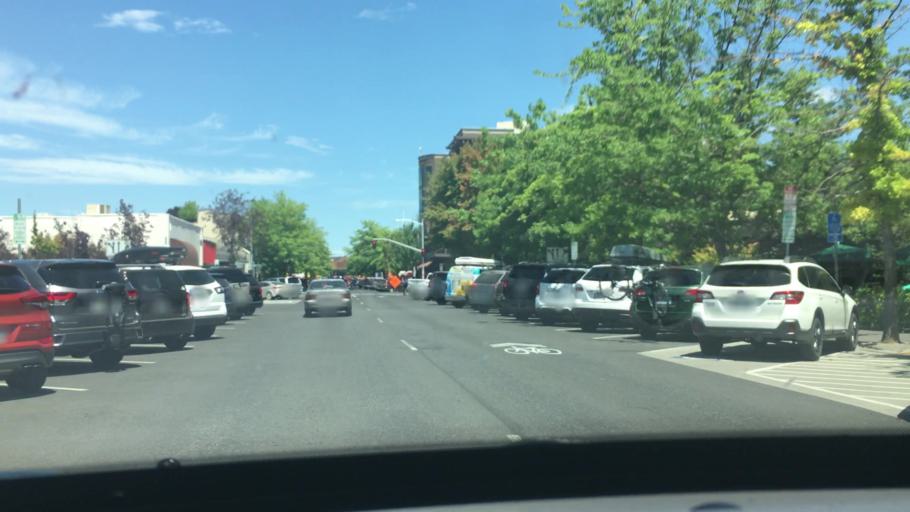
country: US
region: Oregon
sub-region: Deschutes County
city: Bend
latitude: 44.0567
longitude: -121.3148
